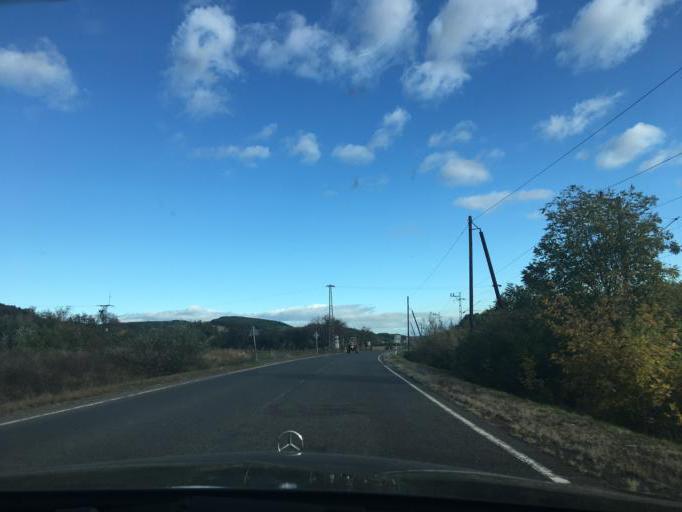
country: HU
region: Borsod-Abauj-Zemplen
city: Gonc
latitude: 48.4771
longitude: 21.2073
